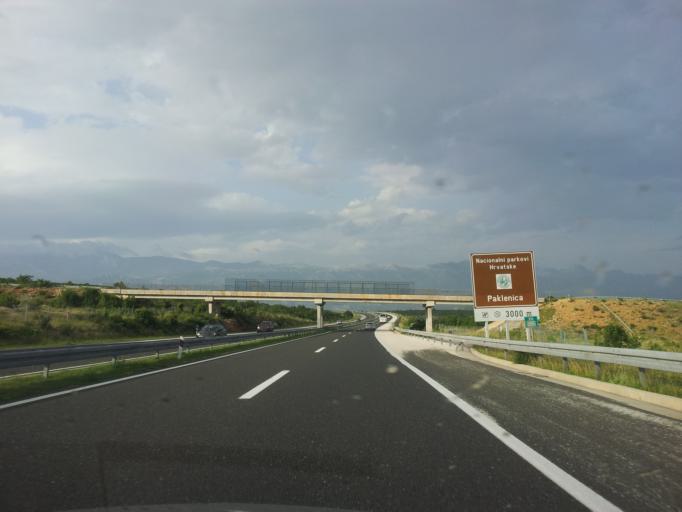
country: HR
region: Zadarska
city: Posedarje
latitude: 44.2206
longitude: 15.5010
